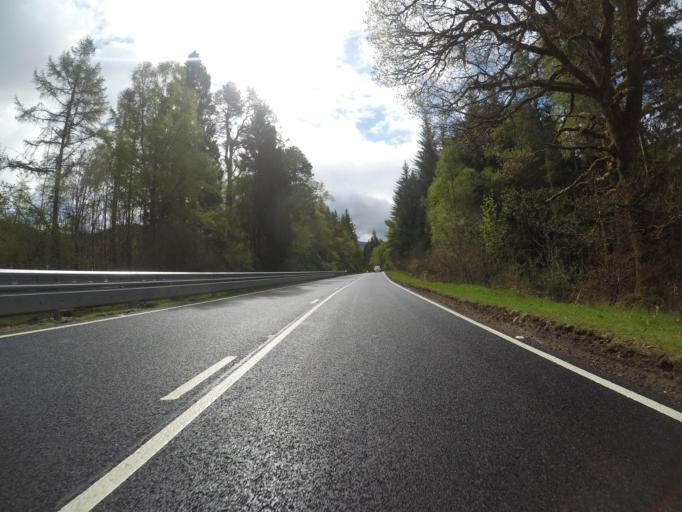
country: GB
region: Scotland
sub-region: Highland
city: Spean Bridge
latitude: 57.0741
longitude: -4.8346
